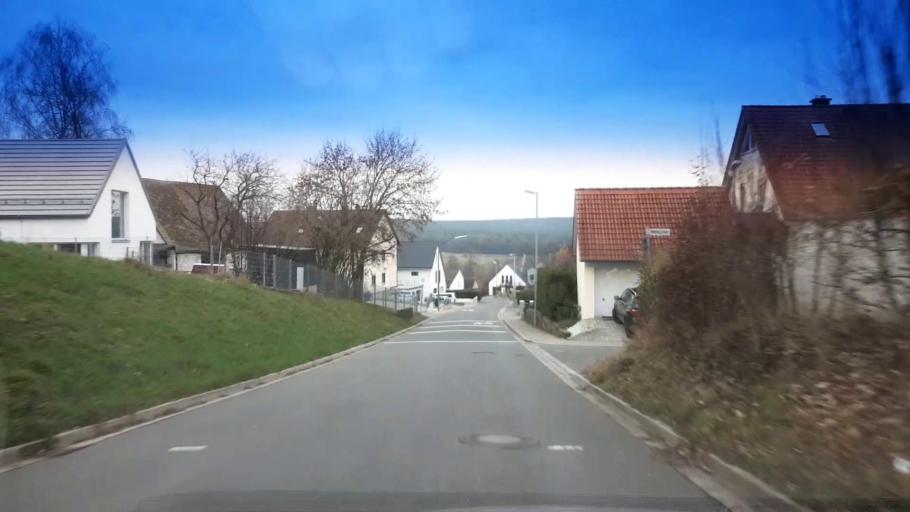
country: DE
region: Bavaria
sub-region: Upper Franconia
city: Hallerndorf
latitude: 49.7606
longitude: 10.9768
